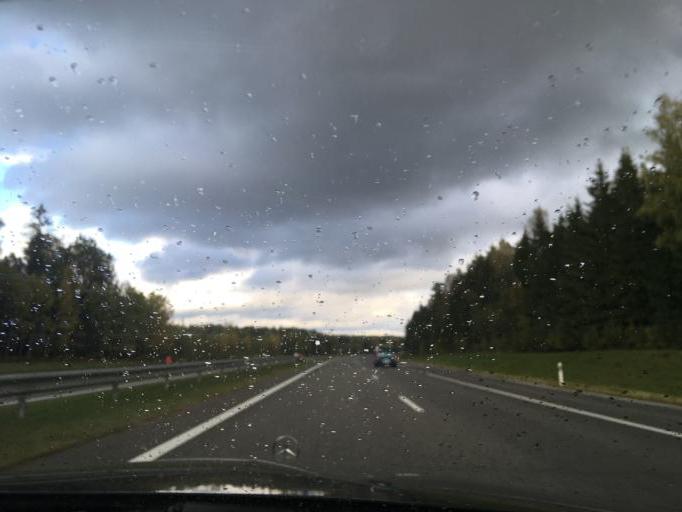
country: BY
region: Vitebsk
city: Talachyn
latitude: 54.4181
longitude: 29.5187
